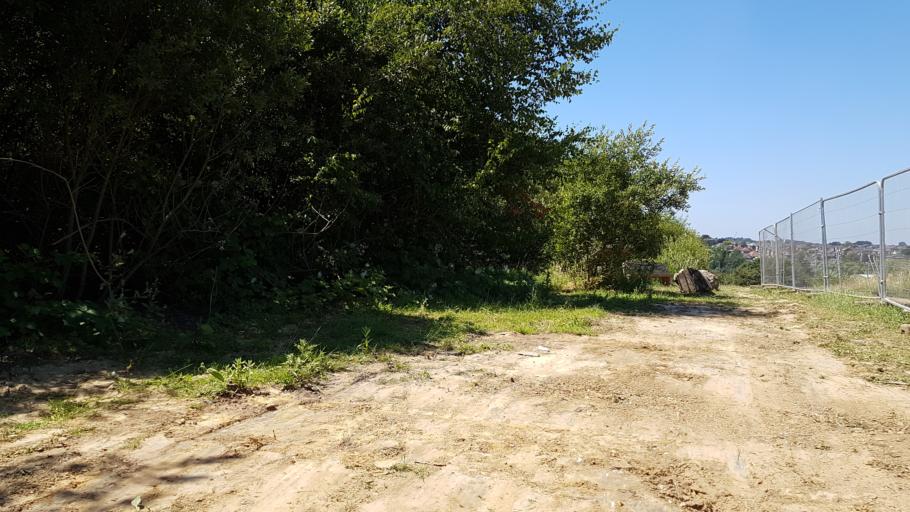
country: GB
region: England
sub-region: Isle of Wight
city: Newport
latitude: 50.6934
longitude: -1.2814
